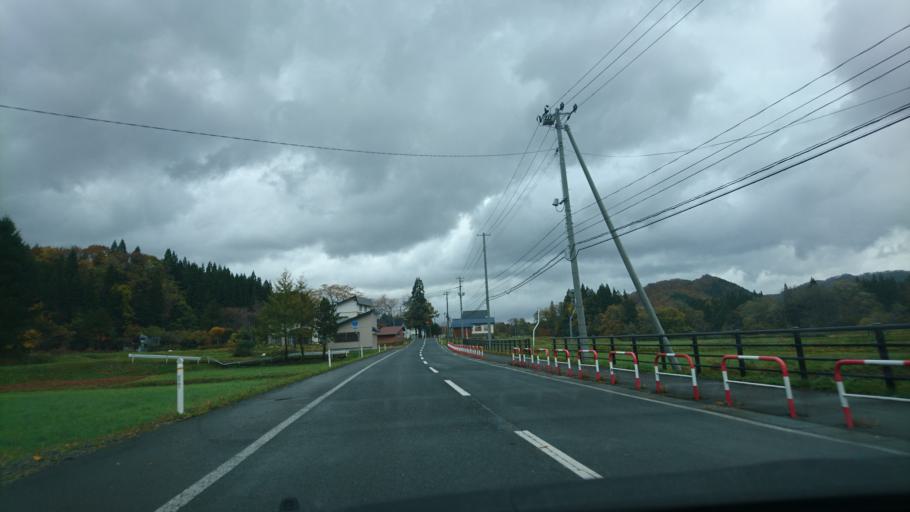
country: JP
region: Iwate
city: Shizukuishi
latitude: 39.5097
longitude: 140.8278
